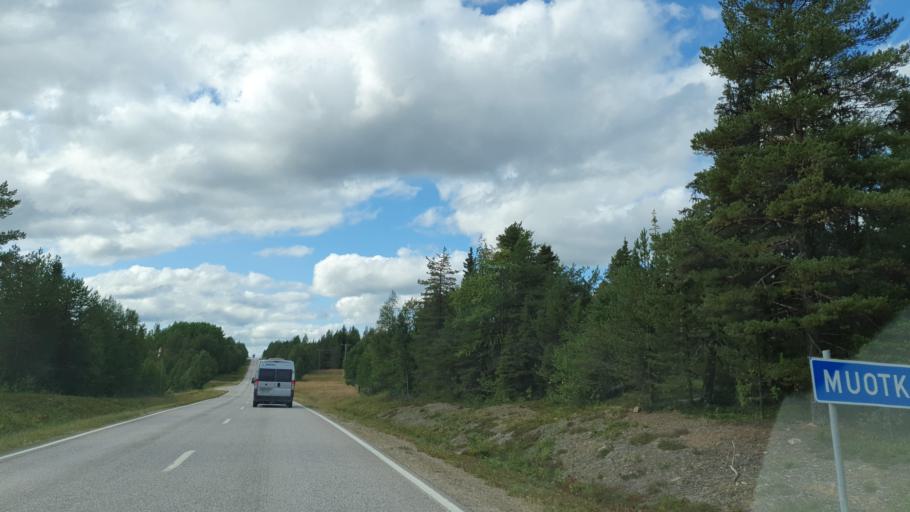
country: FI
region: Lapland
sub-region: Tunturi-Lappi
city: Muonio
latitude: 67.8609
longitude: 24.1246
